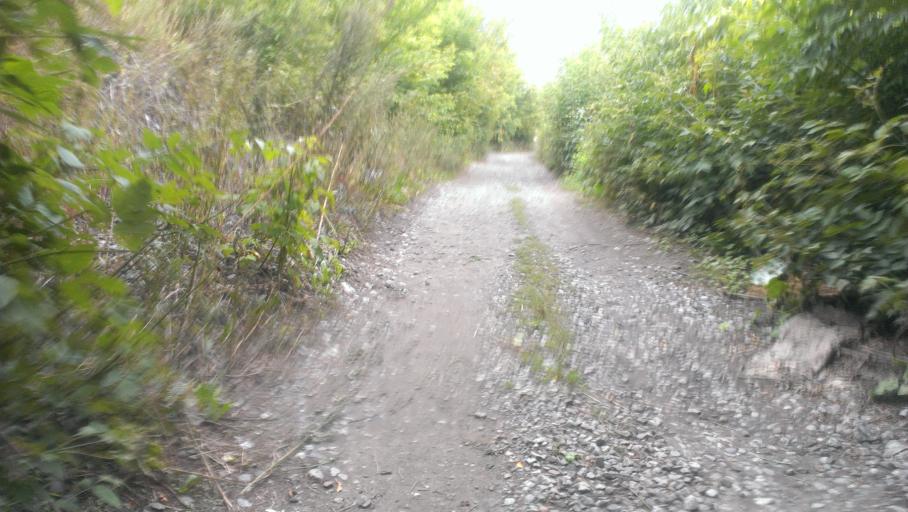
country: RU
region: Altai Krai
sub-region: Gorod Barnaulskiy
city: Barnaul
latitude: 53.3506
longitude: 83.7534
